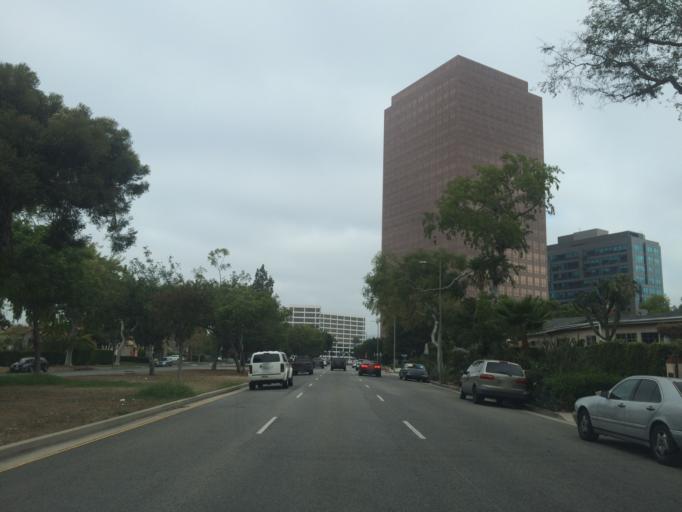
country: US
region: California
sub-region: Los Angeles County
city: West Hollywood
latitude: 34.0622
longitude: -118.3688
